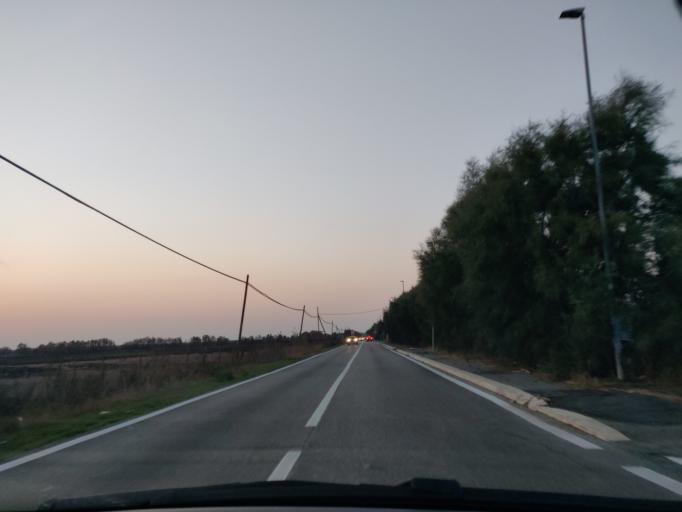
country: IT
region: Latium
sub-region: Citta metropolitana di Roma Capitale
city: Npp 23 (Parco Leonardo)
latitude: 41.8143
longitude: 12.3006
